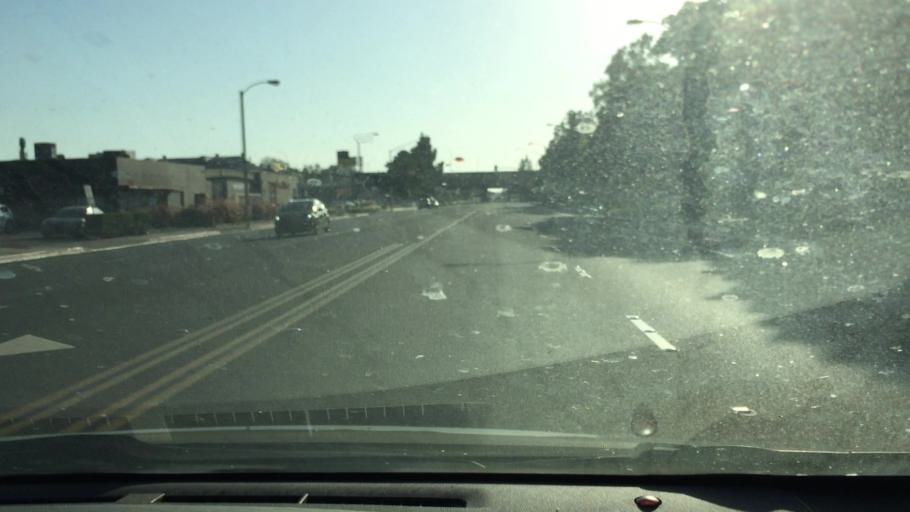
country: US
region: California
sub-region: Orange County
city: Costa Mesa
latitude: 33.6802
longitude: -117.8881
